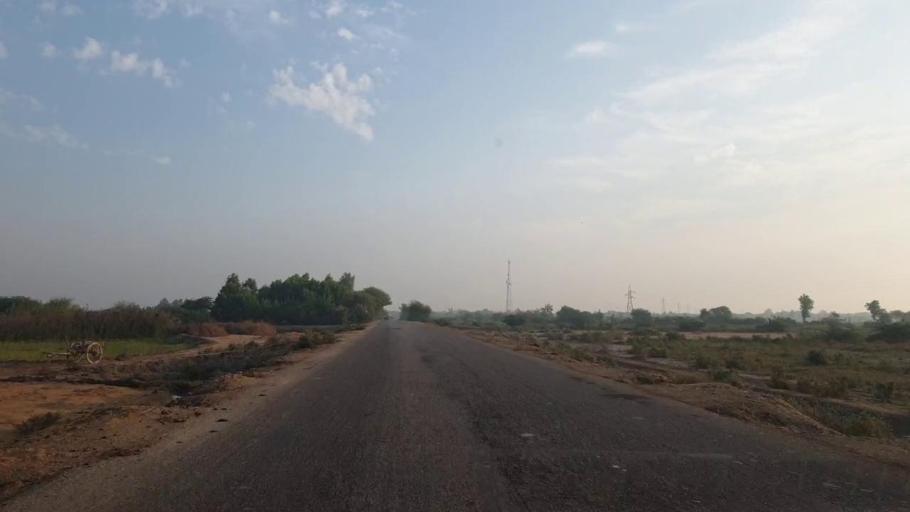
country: PK
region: Sindh
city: Tando Bago
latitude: 24.7035
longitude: 68.9264
